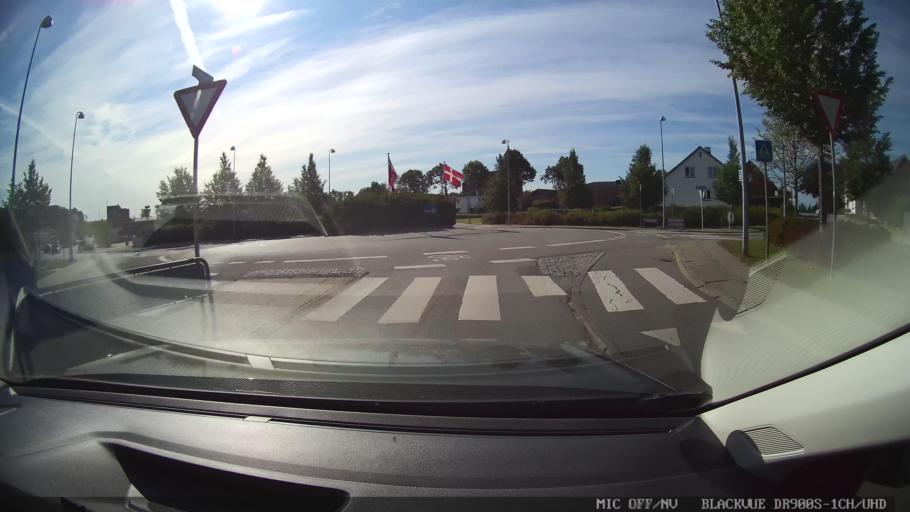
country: DK
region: North Denmark
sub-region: Mariagerfjord Kommune
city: Arden
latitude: 56.7696
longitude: 9.8560
